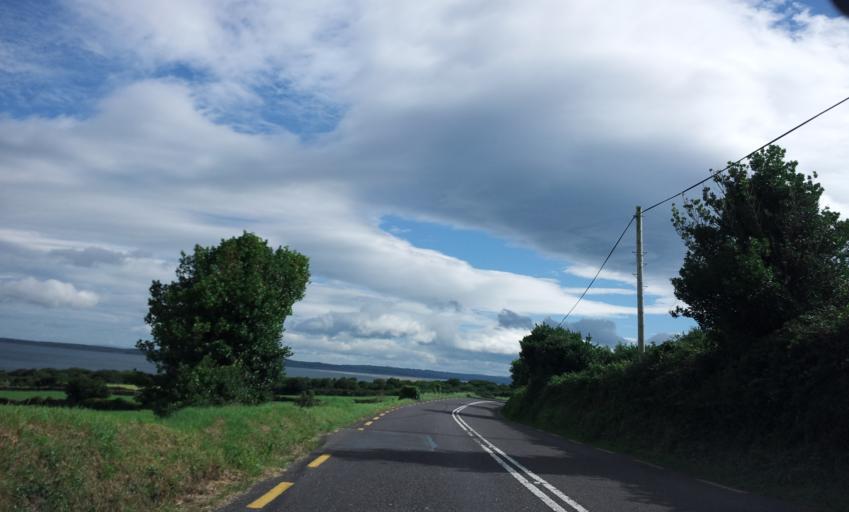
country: IE
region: Munster
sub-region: Ciarrai
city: Killorglin
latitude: 52.2276
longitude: -9.8858
